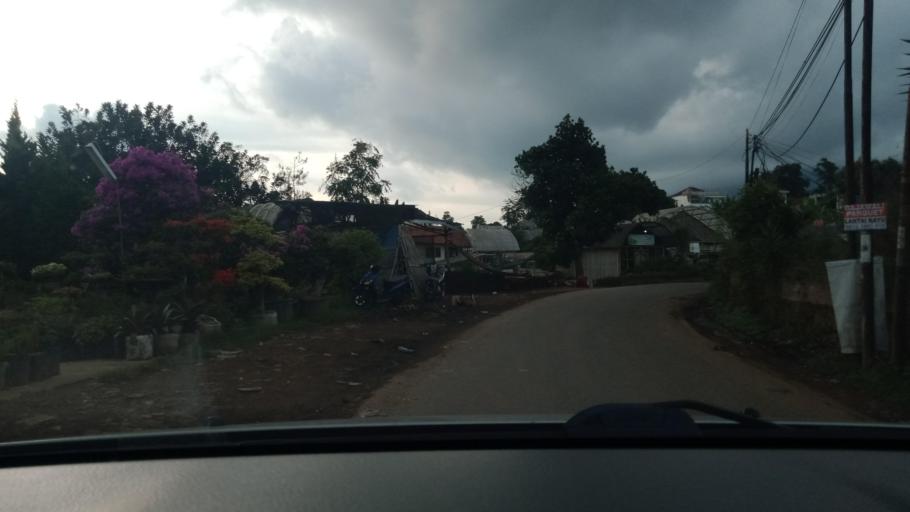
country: ID
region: West Java
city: Lembang
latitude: -6.8079
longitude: 107.5889
